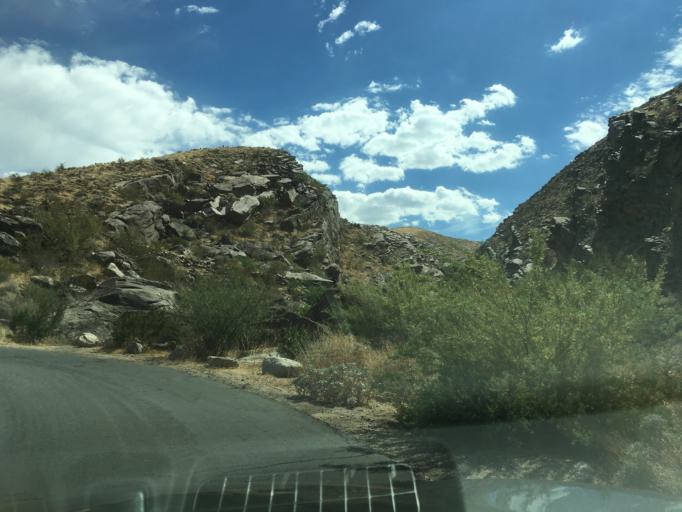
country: US
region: California
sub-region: Riverside County
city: Cathedral City
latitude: 33.7384
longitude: -116.5394
